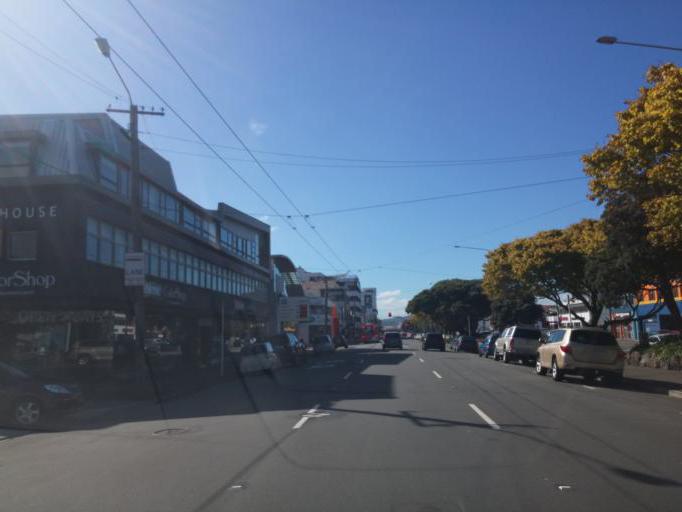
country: NZ
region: Wellington
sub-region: Wellington City
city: Wellington
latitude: -41.2985
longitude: 174.7811
